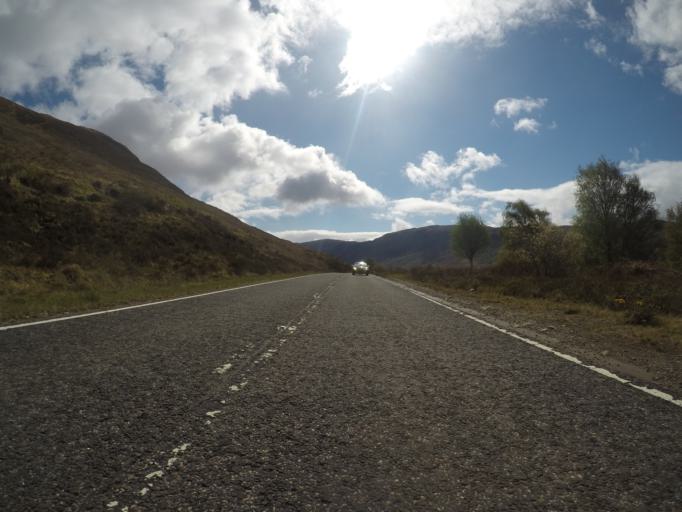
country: GB
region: Scotland
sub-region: Highland
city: Spean Bridge
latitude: 57.1510
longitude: -5.1234
